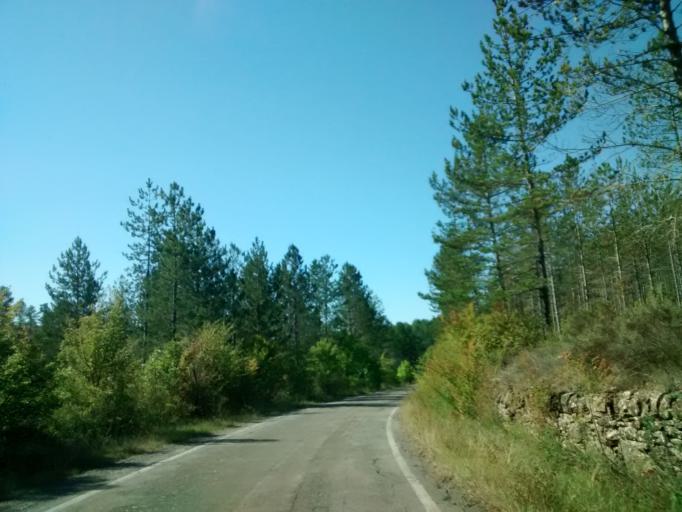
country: ES
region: Aragon
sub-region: Provincia de Huesca
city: Santa Cruz de la Seros
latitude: 42.4564
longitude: -0.6114
